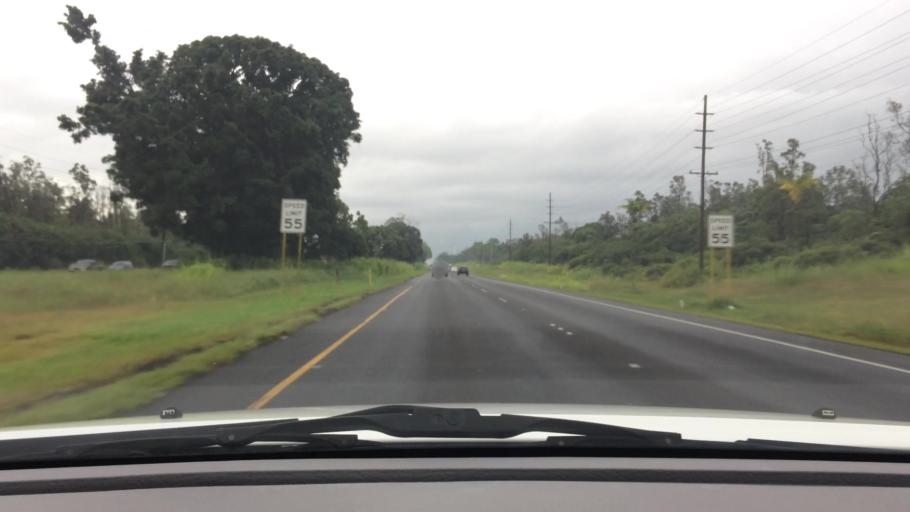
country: US
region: Hawaii
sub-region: Hawaii County
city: Kea'au
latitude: 19.6550
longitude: -155.0549
